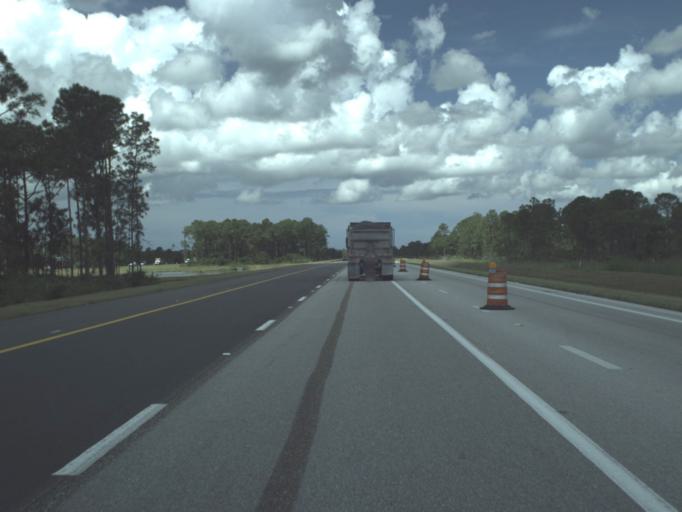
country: US
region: Florida
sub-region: Sarasota County
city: Warm Mineral Springs
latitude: 27.1035
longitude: -82.2913
